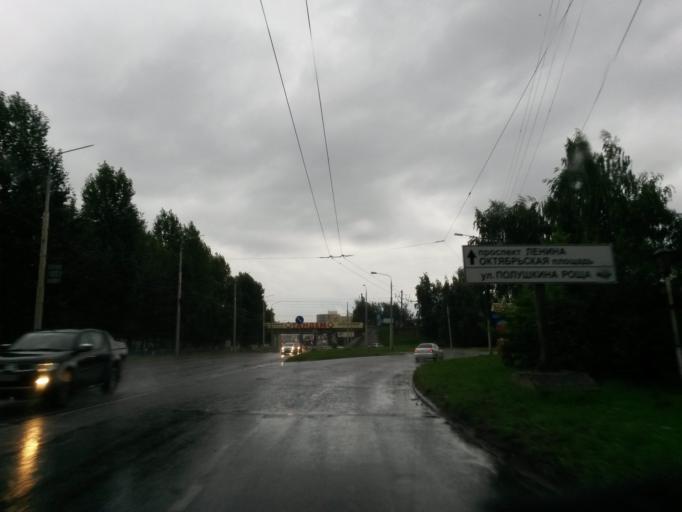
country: RU
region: Jaroslavl
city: Yaroslavl
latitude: 57.6471
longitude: 39.8799
